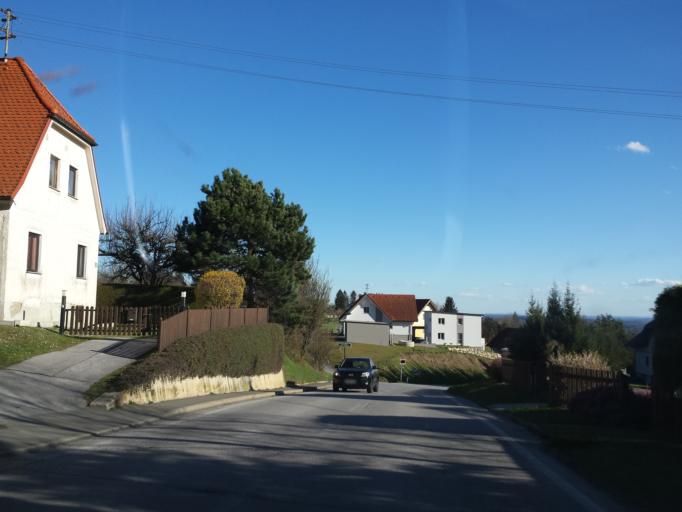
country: AT
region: Styria
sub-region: Politischer Bezirk Graz-Umgebung
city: Sankt Radegund bei Graz
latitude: 47.1602
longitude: 15.4908
